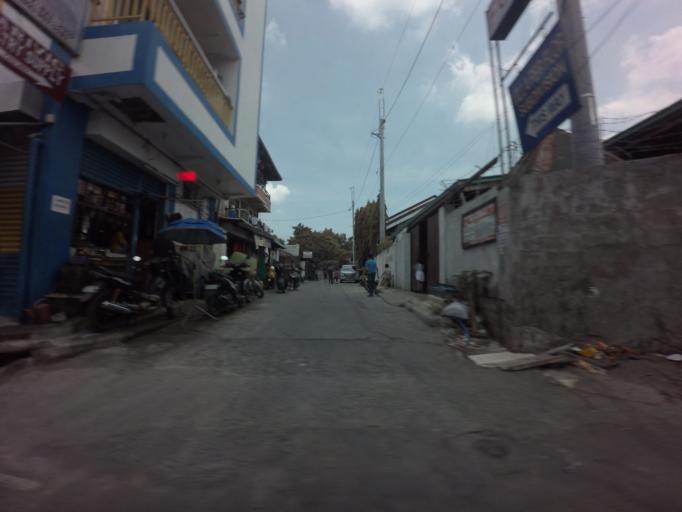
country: PH
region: Calabarzon
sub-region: Province of Rizal
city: Taguig
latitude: 14.4752
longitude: 121.0596
